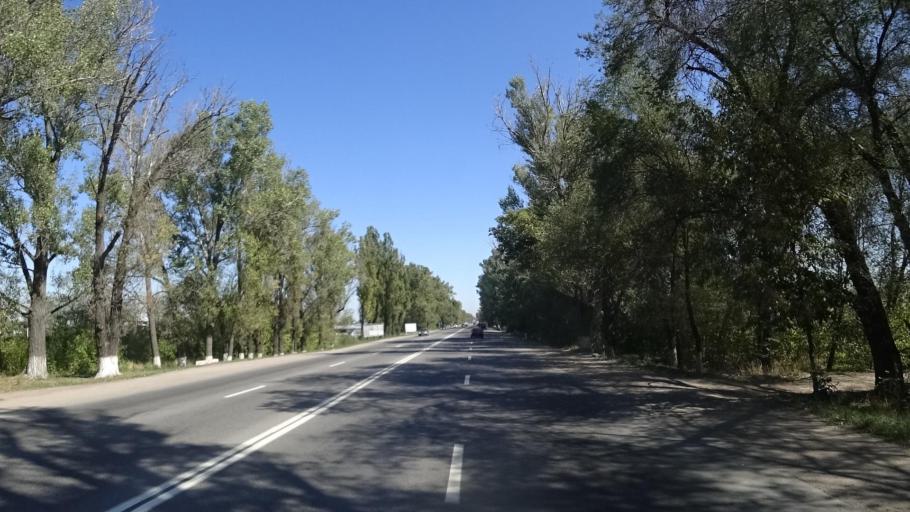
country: KZ
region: Almaty Oblysy
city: Energeticheskiy
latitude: 43.3612
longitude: 77.0787
